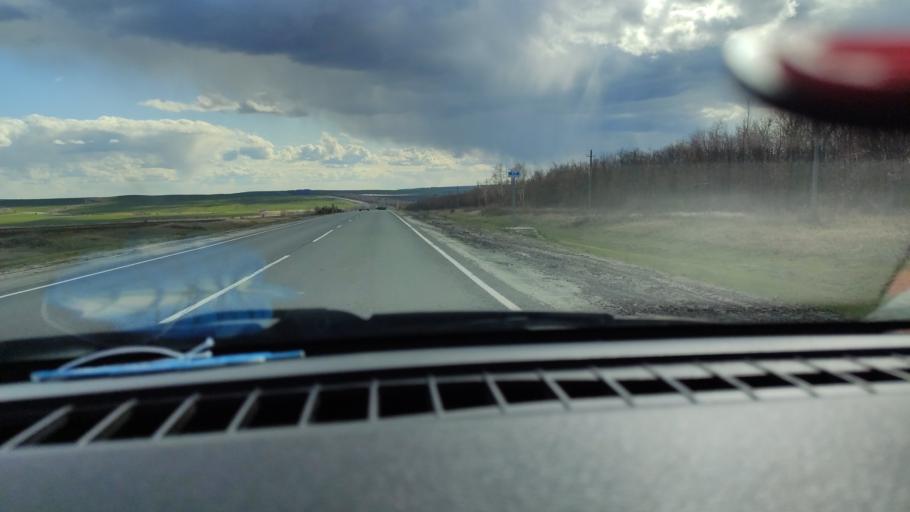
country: RU
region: Saratov
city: Alekseyevka
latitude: 52.2593
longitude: 47.9196
